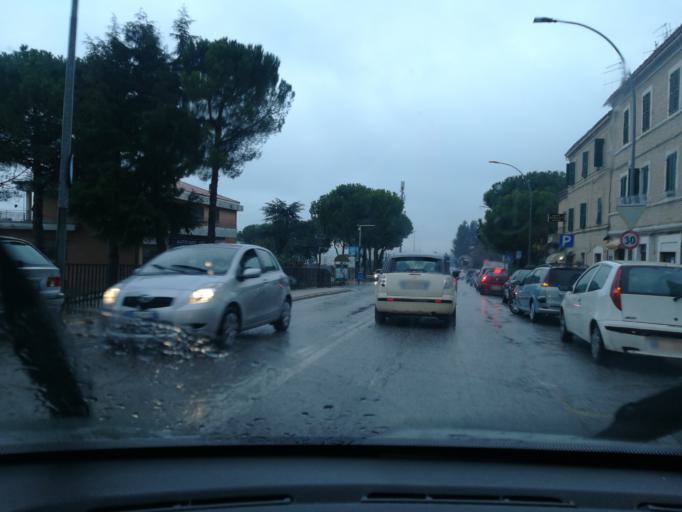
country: IT
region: The Marches
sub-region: Provincia di Macerata
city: Macerata
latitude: 43.2893
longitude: 13.4355
